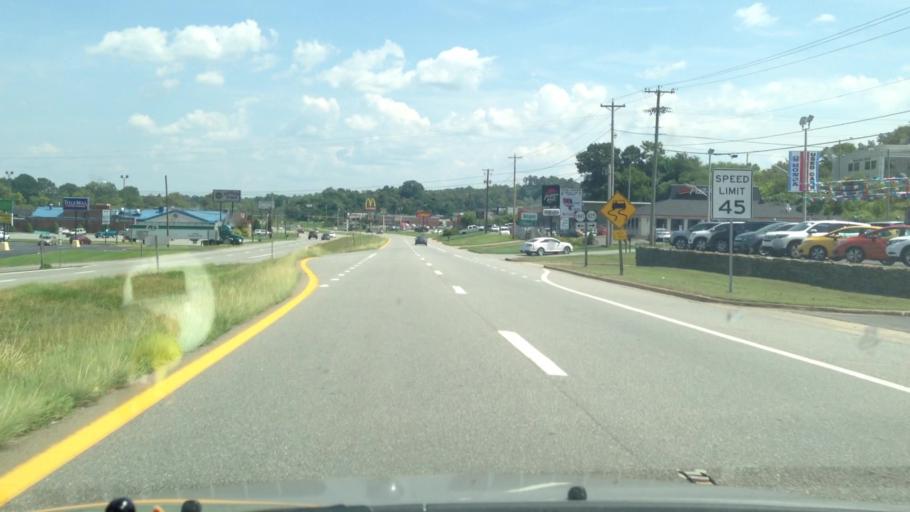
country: US
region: Virginia
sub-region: City of Martinsville
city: Martinsville
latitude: 36.6562
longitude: -79.8780
